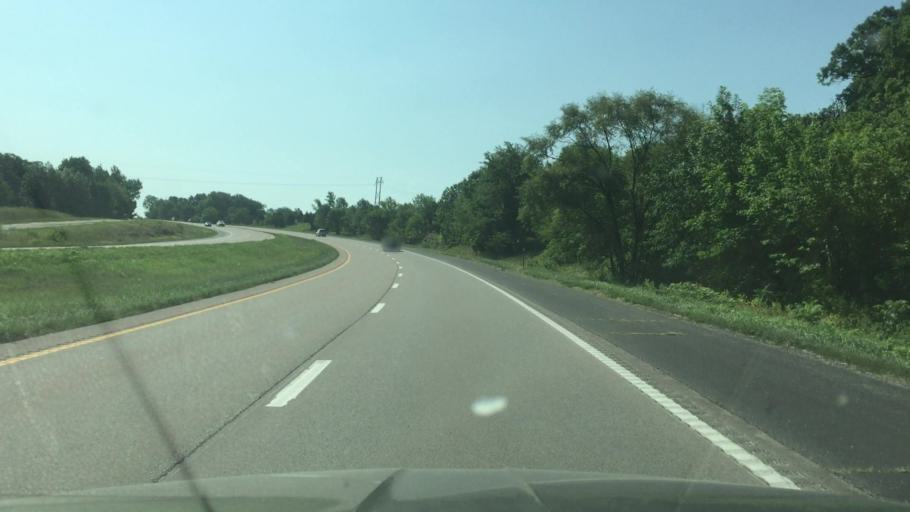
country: US
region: Missouri
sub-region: Pettis County
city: Sedalia
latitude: 38.7219
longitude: -93.3003
